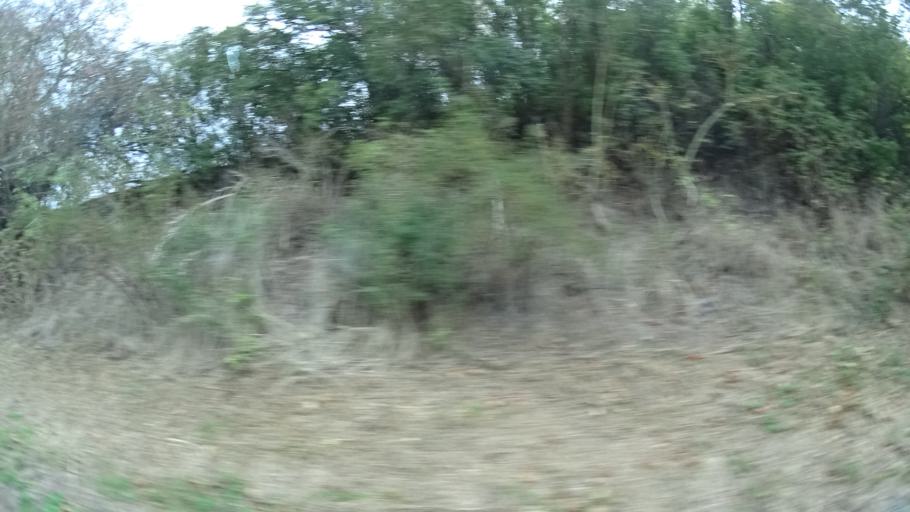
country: DE
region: Thuringia
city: Wasungen
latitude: 50.6712
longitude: 10.3552
